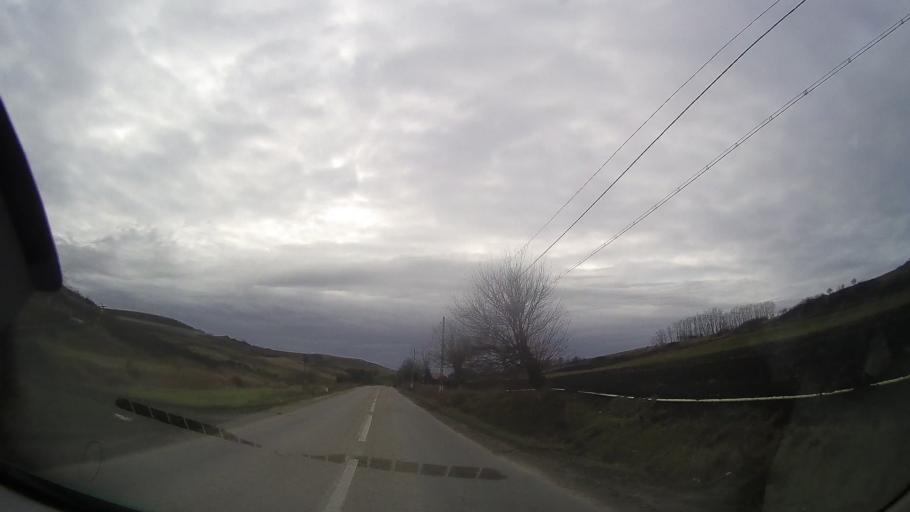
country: RO
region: Bistrita-Nasaud
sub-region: Comuna Budesti
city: Budesti
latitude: 46.8550
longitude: 24.2434
